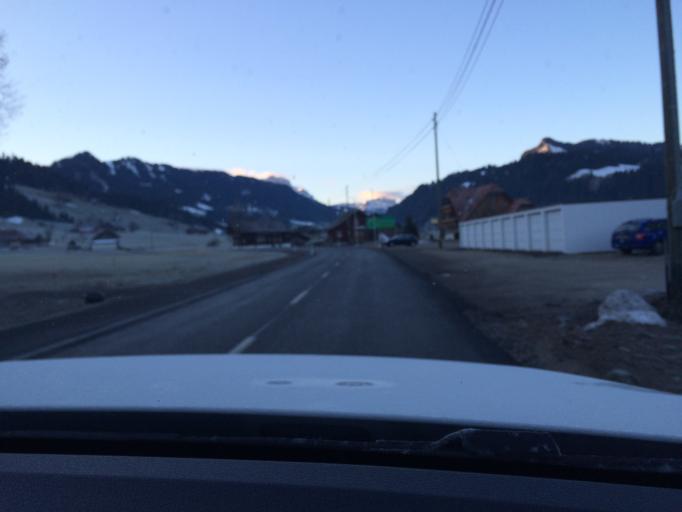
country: CH
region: Lucerne
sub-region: Entlebuch District
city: Escholzmatt
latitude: 46.8733
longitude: 7.9107
